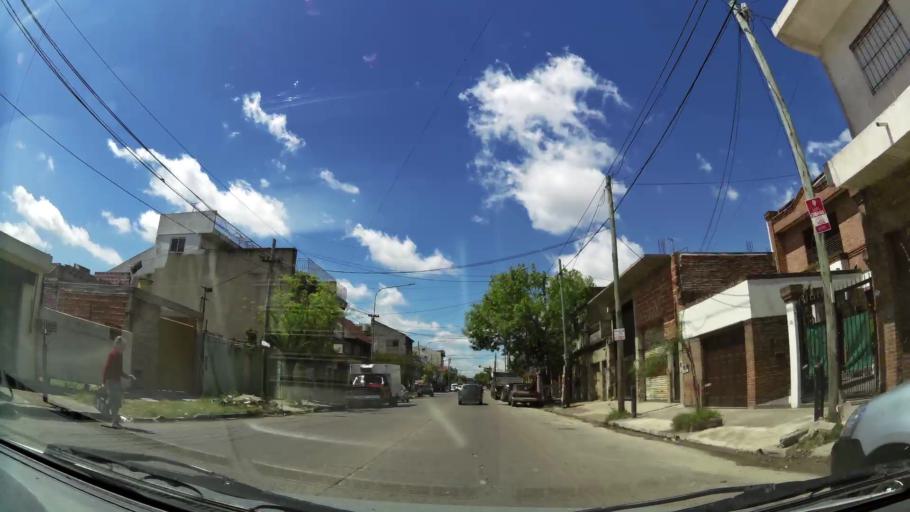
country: AR
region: Buenos Aires
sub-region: Partido de Lanus
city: Lanus
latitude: -34.7017
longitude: -58.4179
